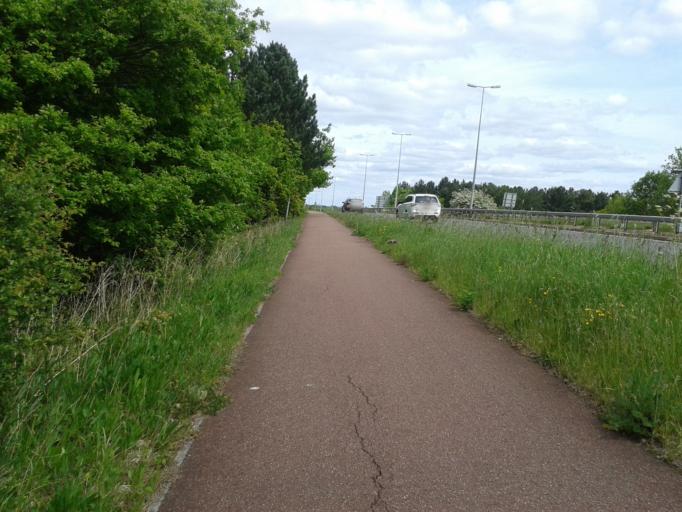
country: GB
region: England
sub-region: Cambridgeshire
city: Barton
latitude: 52.1878
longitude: 0.0731
